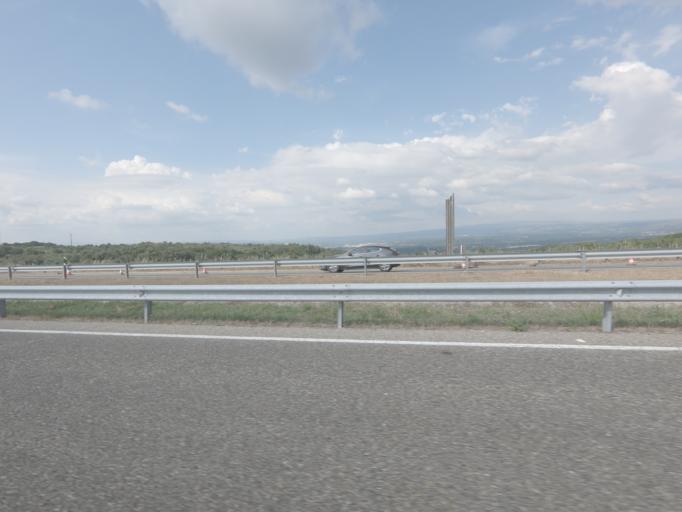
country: ES
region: Galicia
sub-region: Provincia de Ourense
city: Taboadela
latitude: 42.2376
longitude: -7.8569
